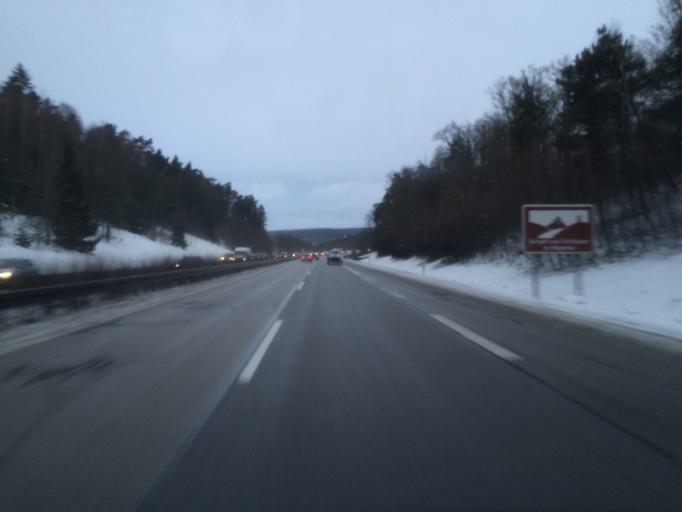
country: DE
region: Bavaria
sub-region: Upper Palatinate
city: Zeitlarn
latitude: 49.0903
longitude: 12.0963
